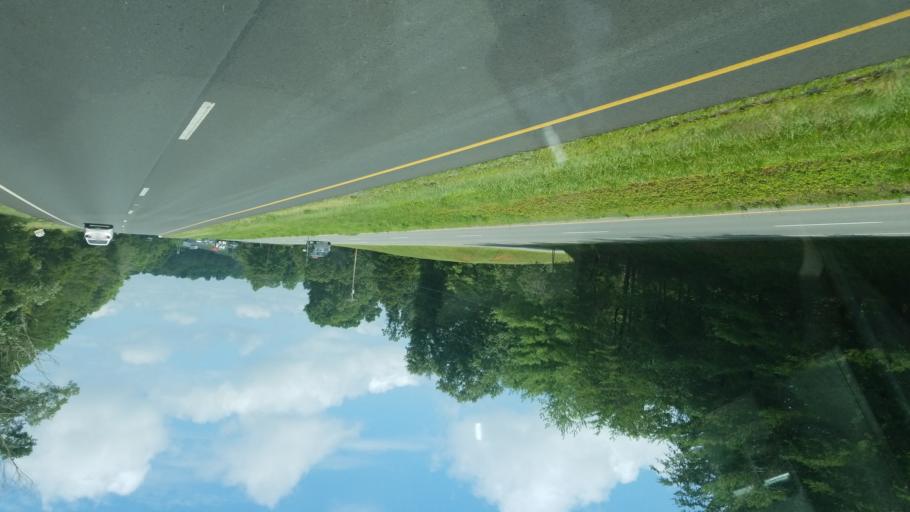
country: US
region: Virginia
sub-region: Fauquier County
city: Bealeton
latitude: 38.4935
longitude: -77.6858
